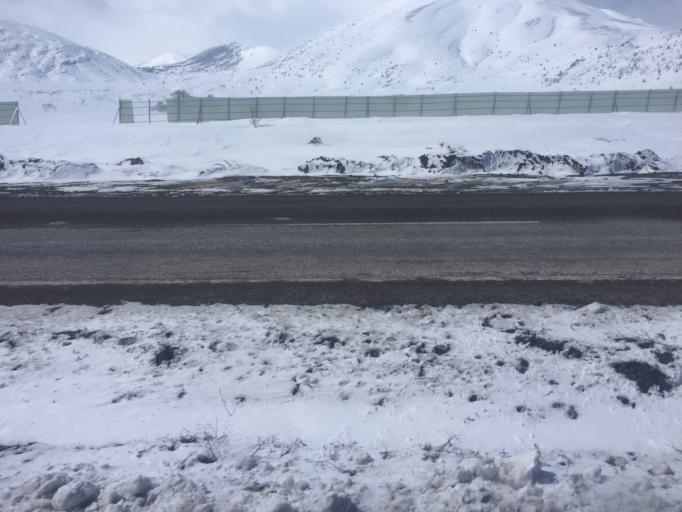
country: TR
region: Kahramanmaras
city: Goksun
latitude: 38.1773
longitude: 36.4595
